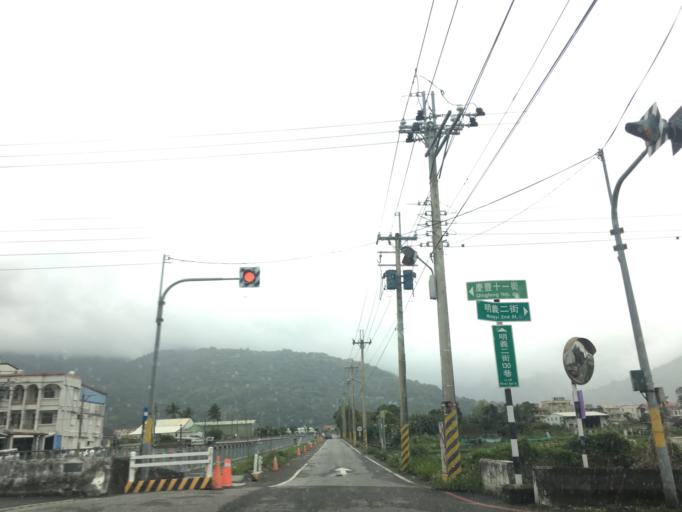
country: TW
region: Taiwan
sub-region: Hualien
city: Hualian
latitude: 23.9846
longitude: 121.5674
